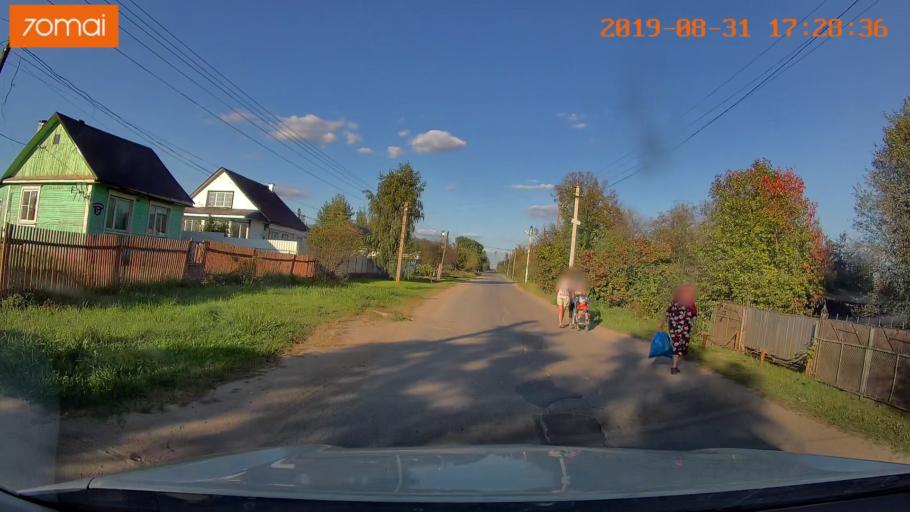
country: RU
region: Kaluga
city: Detchino
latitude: 54.8129
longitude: 36.3194
